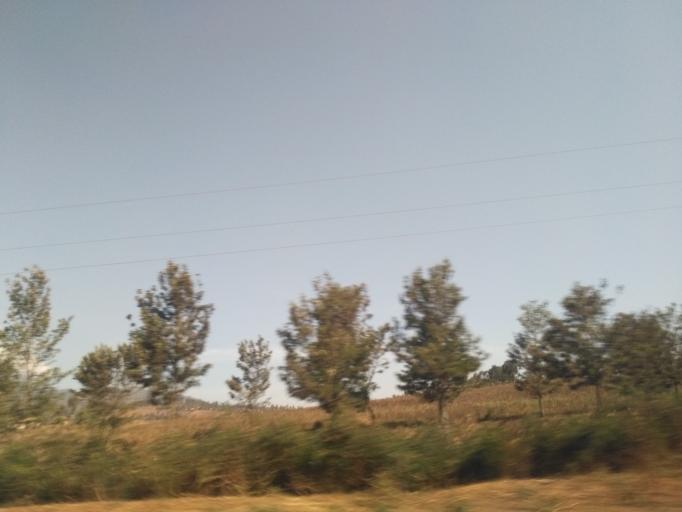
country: TZ
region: Arusha
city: Arusha
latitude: -3.2111
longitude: 36.6182
